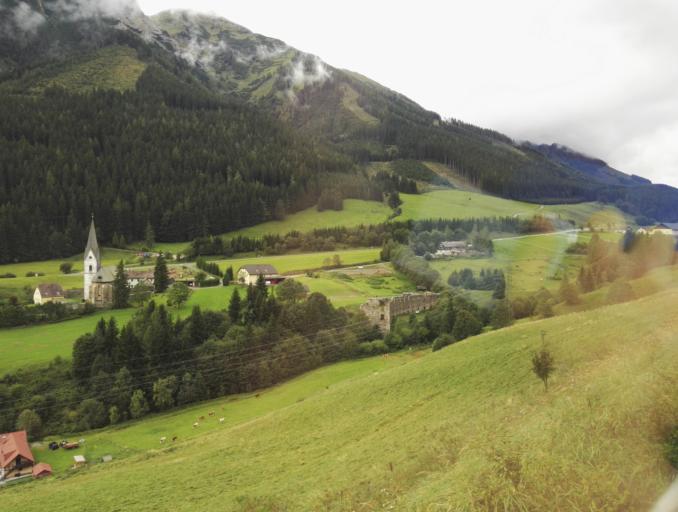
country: AT
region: Styria
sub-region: Politischer Bezirk Leoben
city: Vordernberg
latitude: 47.5019
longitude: 14.9905
